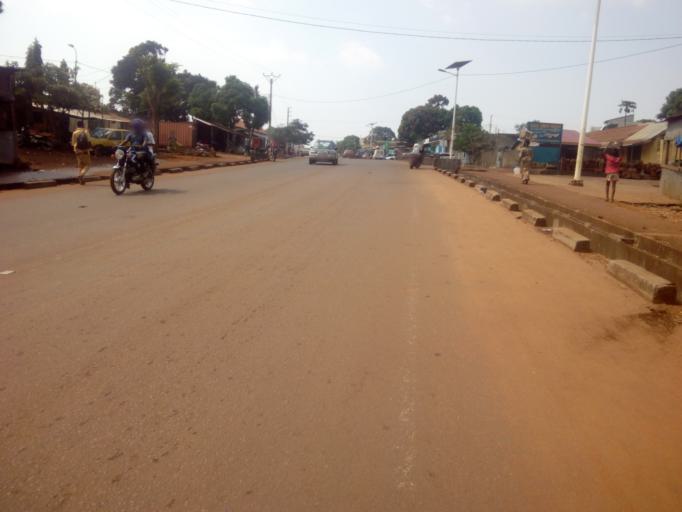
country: GN
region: Conakry
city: Conakry
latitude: 9.6371
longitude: -13.5752
